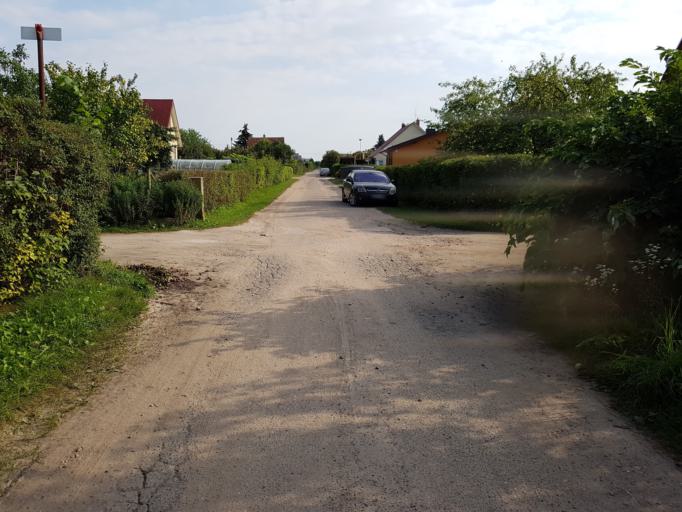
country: LT
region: Vilnius County
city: Rasos
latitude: 54.7893
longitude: 25.3608
